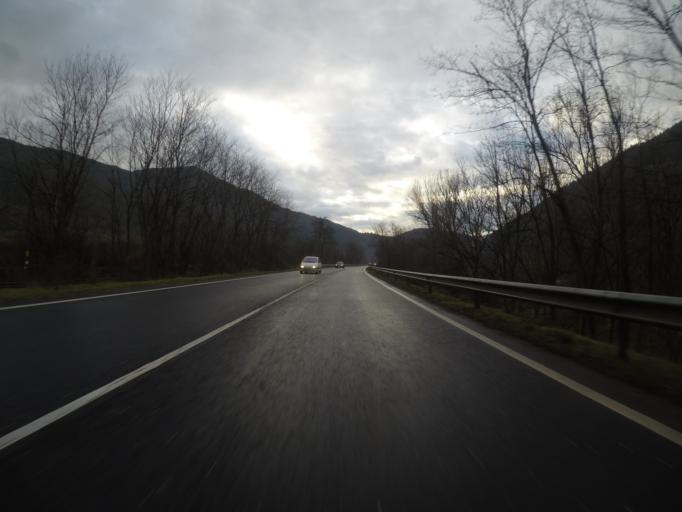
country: BG
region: Blagoevgrad
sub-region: Obshtina Blagoevgrad
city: Blagoevgrad
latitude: 41.9590
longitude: 23.1038
